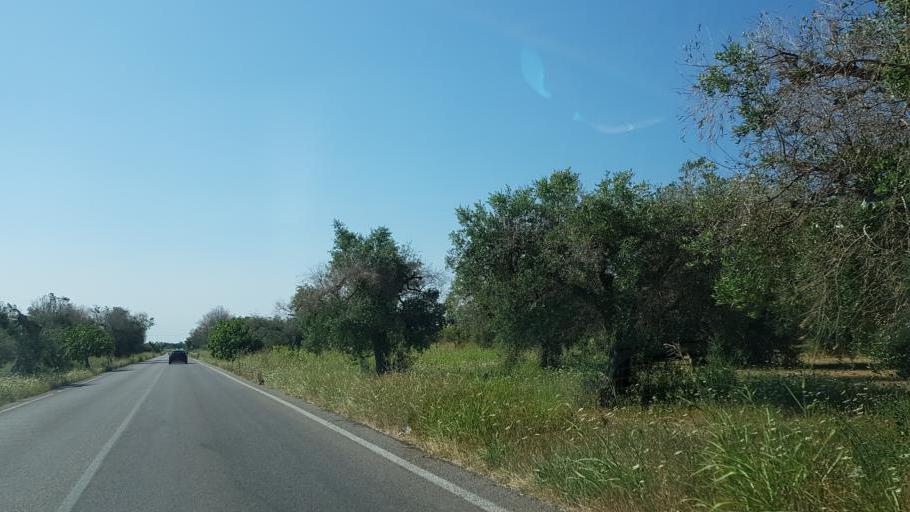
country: IT
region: Apulia
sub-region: Provincia di Lecce
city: Guagnano
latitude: 40.4037
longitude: 17.9682
